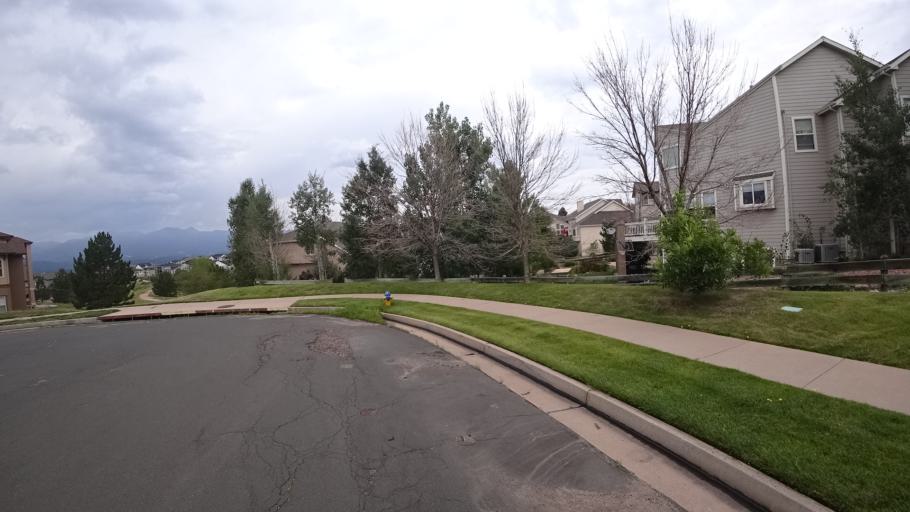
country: US
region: Colorado
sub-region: El Paso County
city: Gleneagle
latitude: 39.0044
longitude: -104.8002
